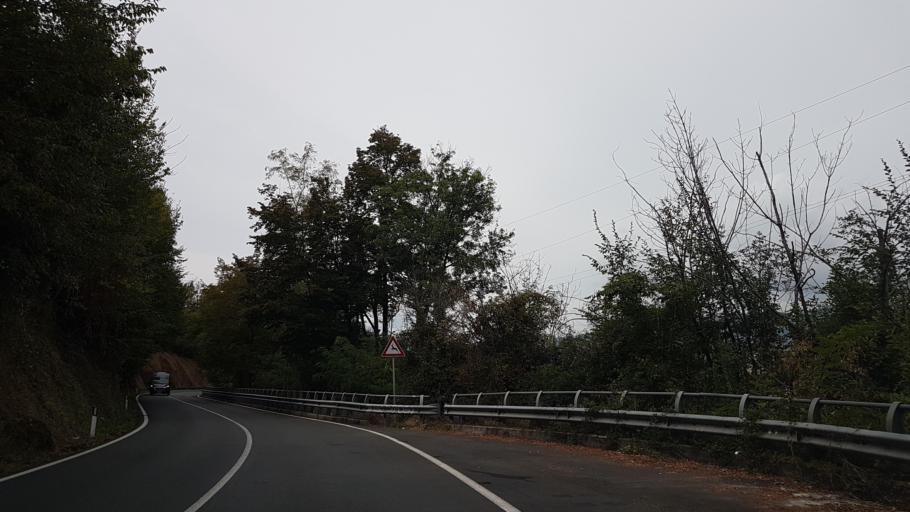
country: IT
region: Liguria
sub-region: Provincia di Genova
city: Casarza Ligure
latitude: 44.2616
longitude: 9.4493
